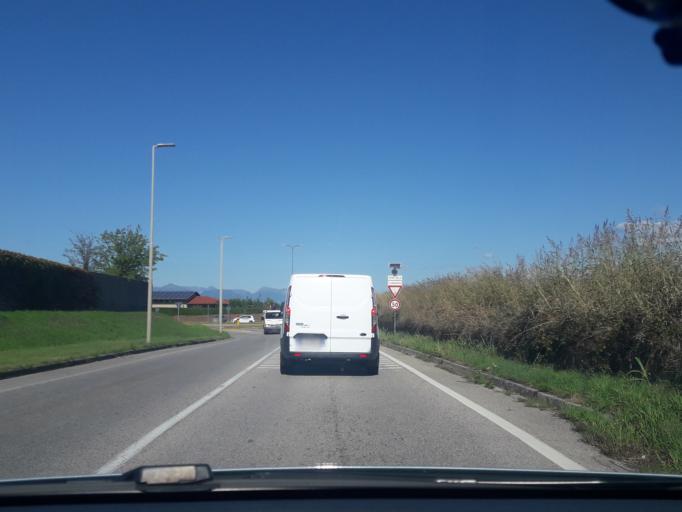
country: IT
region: Friuli Venezia Giulia
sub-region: Provincia di Udine
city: Basaldella
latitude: 46.0284
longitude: 13.2380
